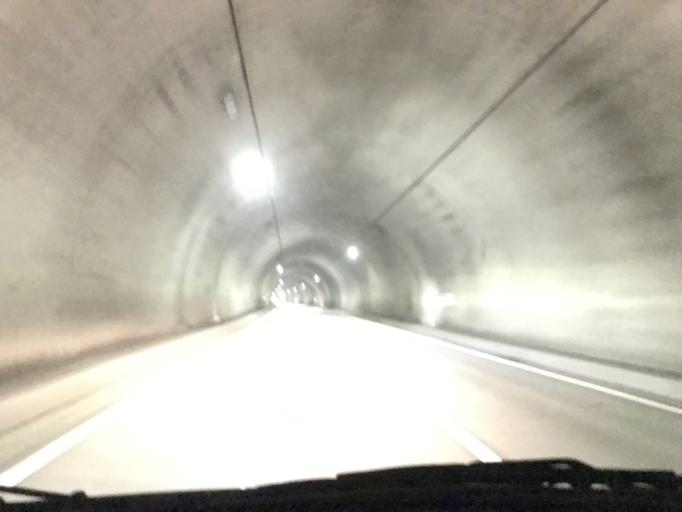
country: JP
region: Iwate
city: Kitakami
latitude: 39.2880
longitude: 141.2506
